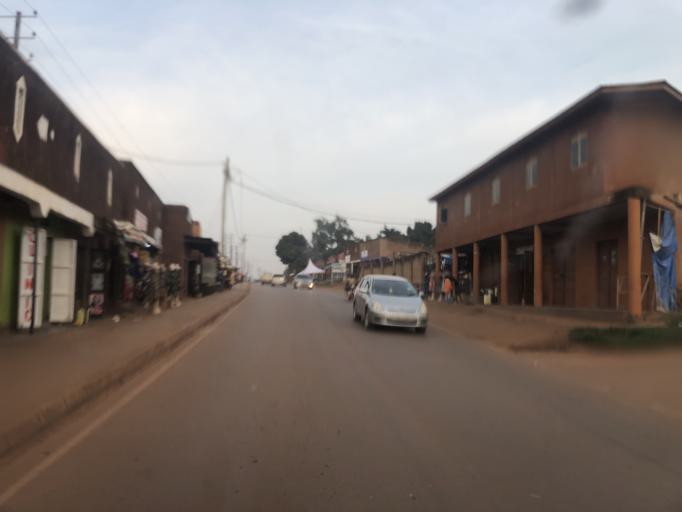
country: UG
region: Central Region
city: Kampala Central Division
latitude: 0.2938
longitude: 32.5298
